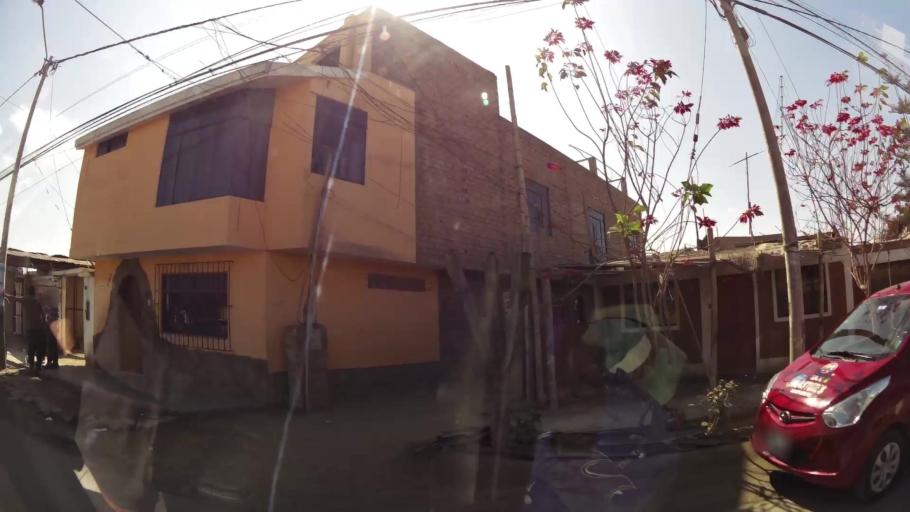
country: PE
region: Ica
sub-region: Provincia de Chincha
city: Sunampe
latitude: -13.4259
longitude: -76.1600
